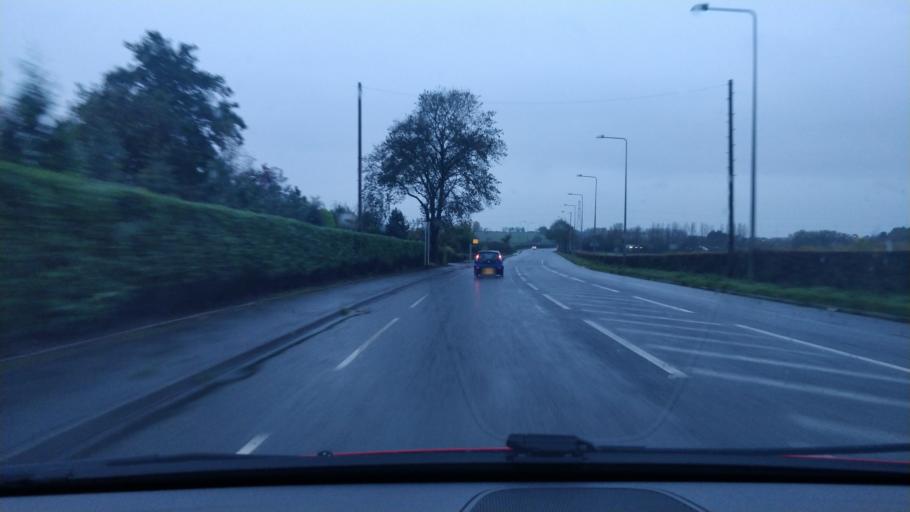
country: GB
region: England
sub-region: Lancashire
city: Poulton le Fylde
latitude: 53.7859
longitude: -2.9597
